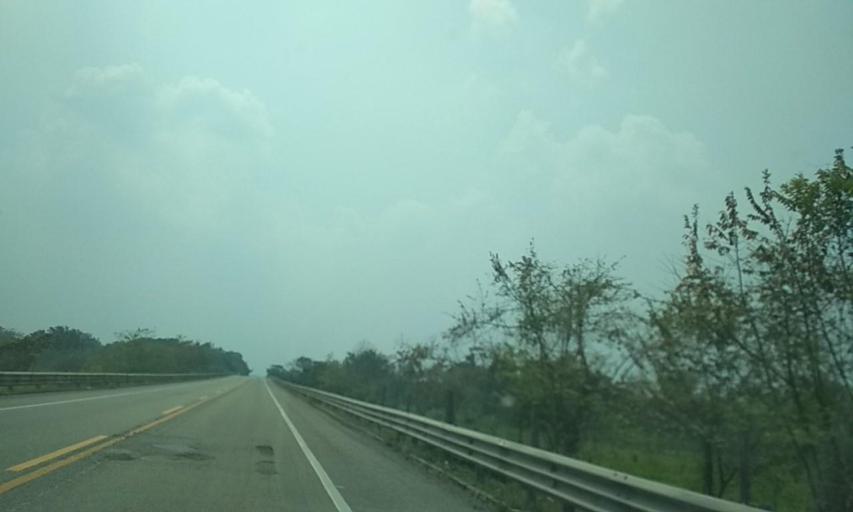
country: MX
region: Tabasco
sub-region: Huimanguillo
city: Francisco Rueda
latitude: 17.7645
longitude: -94.0205
